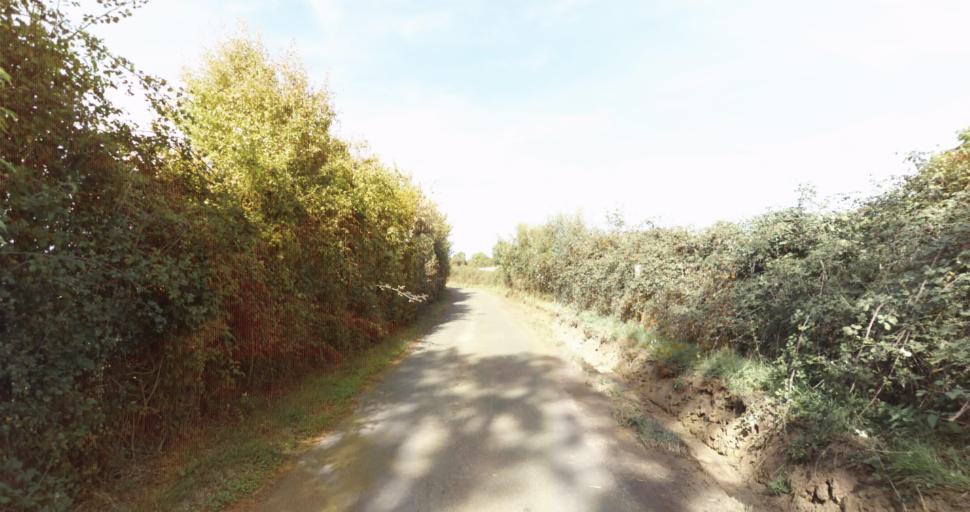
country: FR
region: Lower Normandy
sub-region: Departement de l'Orne
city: Gace
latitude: 48.7118
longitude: 0.2207
